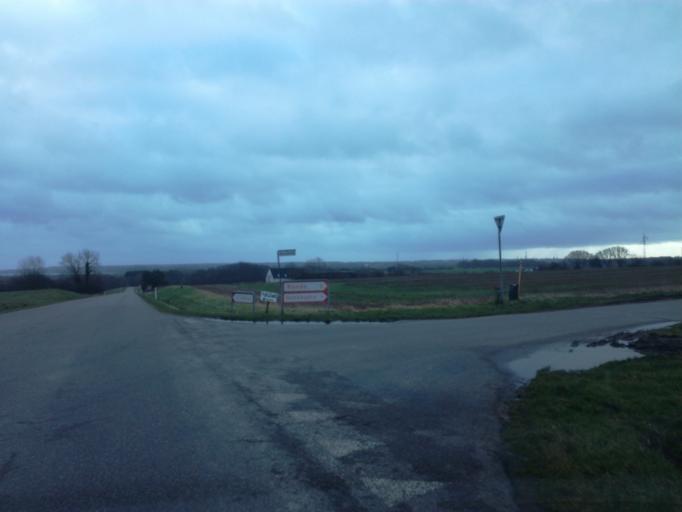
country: DK
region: South Denmark
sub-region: Vejle Kommune
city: Brejning
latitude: 55.6336
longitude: 9.6991
